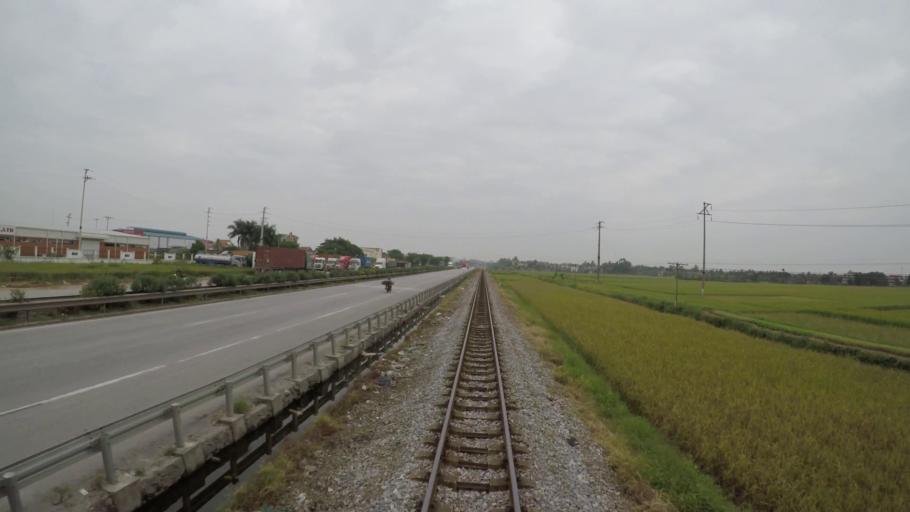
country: VN
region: Hai Duong
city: Phu Thai
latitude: 20.9617
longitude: 106.5196
